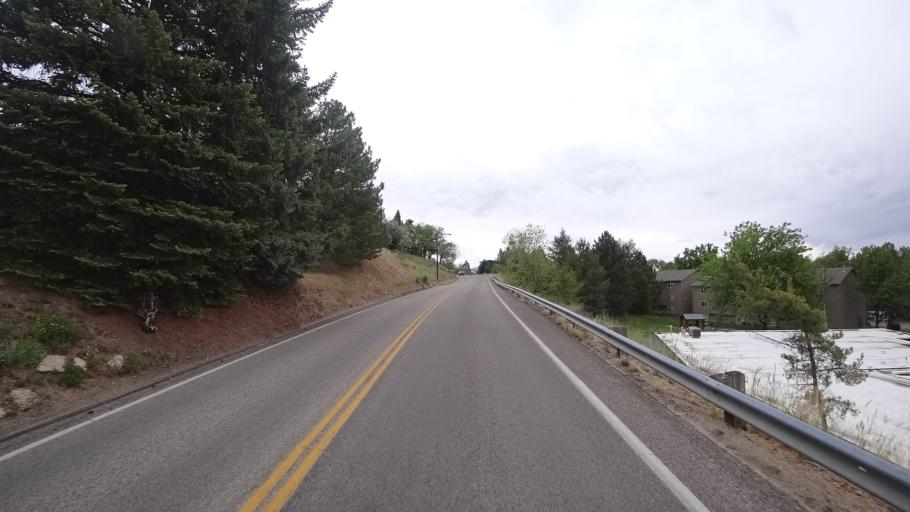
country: US
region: Idaho
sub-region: Ada County
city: Boise
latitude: 43.6151
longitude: -116.1816
